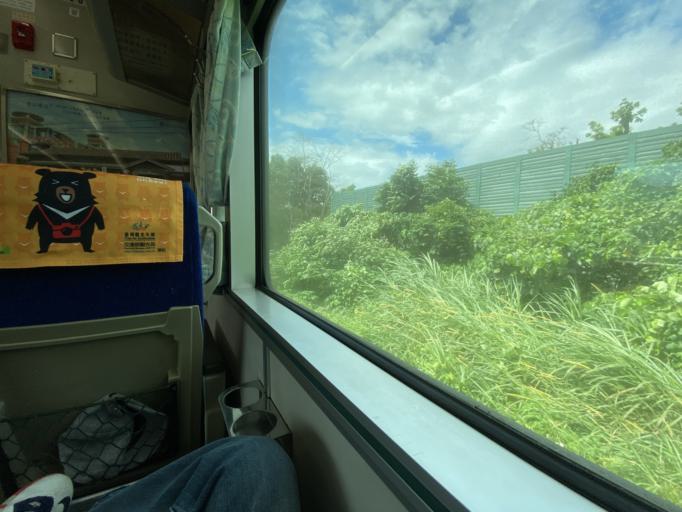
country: TW
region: Taiwan
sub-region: Taitung
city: Taitung
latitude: 22.9091
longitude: 121.1374
